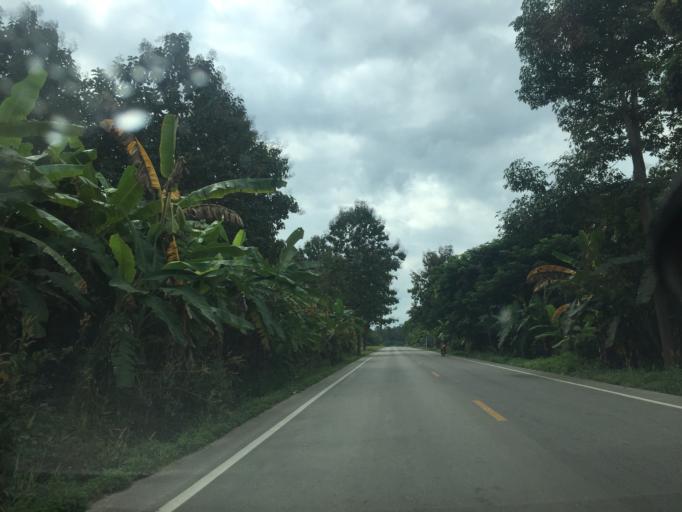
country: TH
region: Lampang
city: Mueang Pan
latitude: 18.7463
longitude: 99.5116
